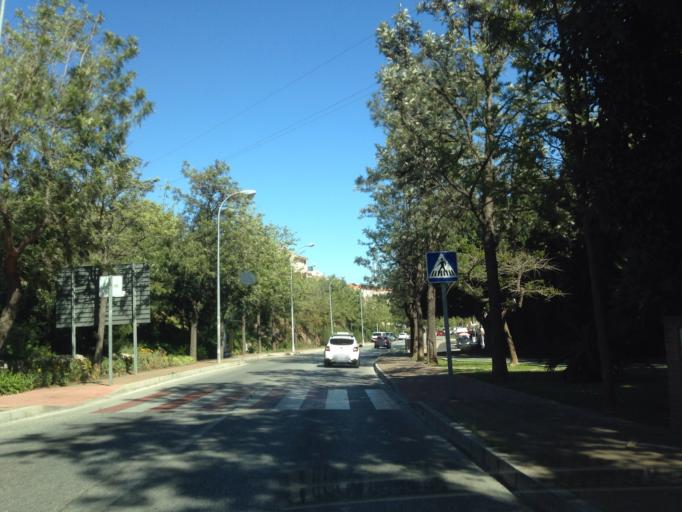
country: ES
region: Andalusia
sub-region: Provincia de Malaga
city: Benalmadena
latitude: 36.6017
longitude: -4.5491
